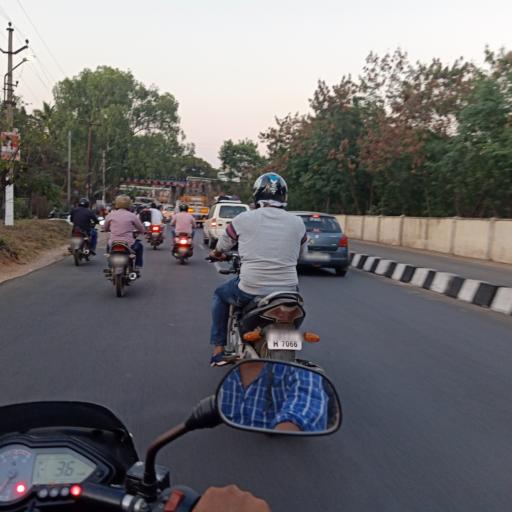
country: IN
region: Telangana
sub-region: Rangareddi
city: Secunderabad
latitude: 17.4905
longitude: 78.5127
